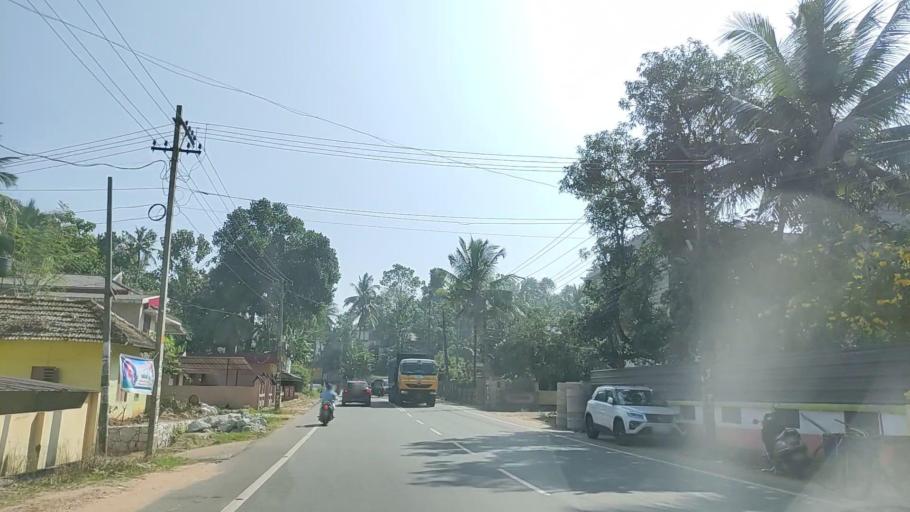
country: IN
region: Kerala
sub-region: Kollam
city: Punalur
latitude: 8.9327
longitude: 76.9386
